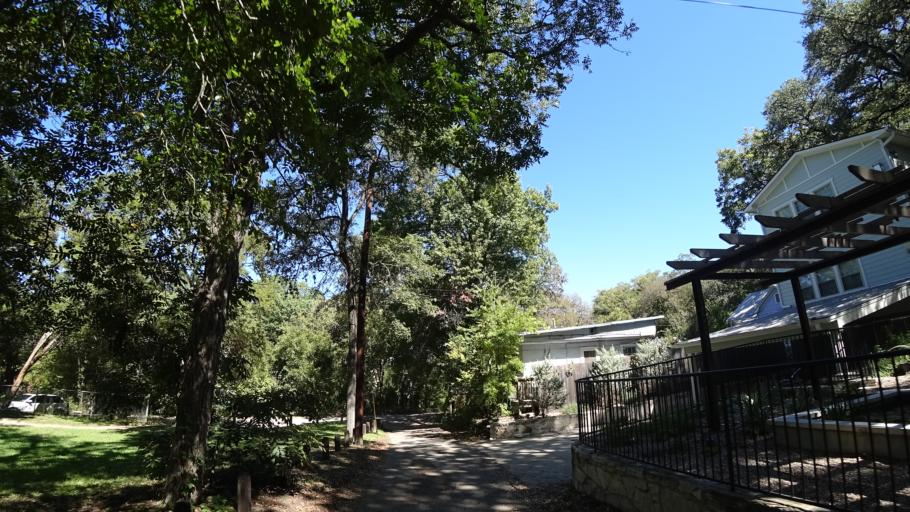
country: US
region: Texas
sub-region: Travis County
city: Austin
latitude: 30.2480
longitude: -97.7428
